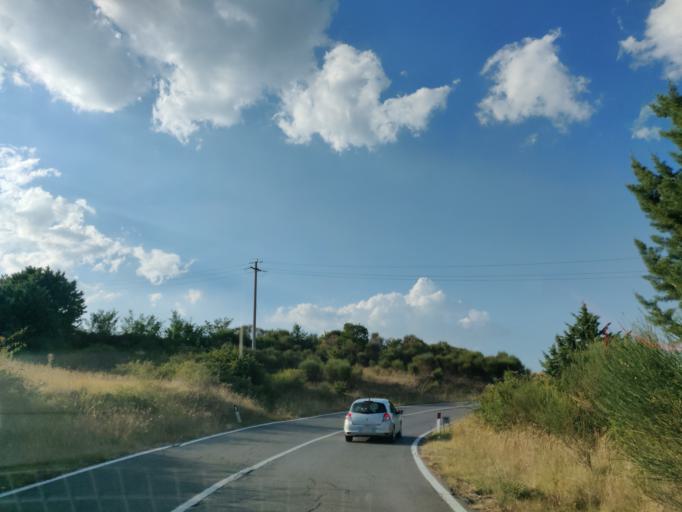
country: IT
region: Tuscany
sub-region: Provincia di Siena
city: Piancastagnaio
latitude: 42.8380
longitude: 11.7117
